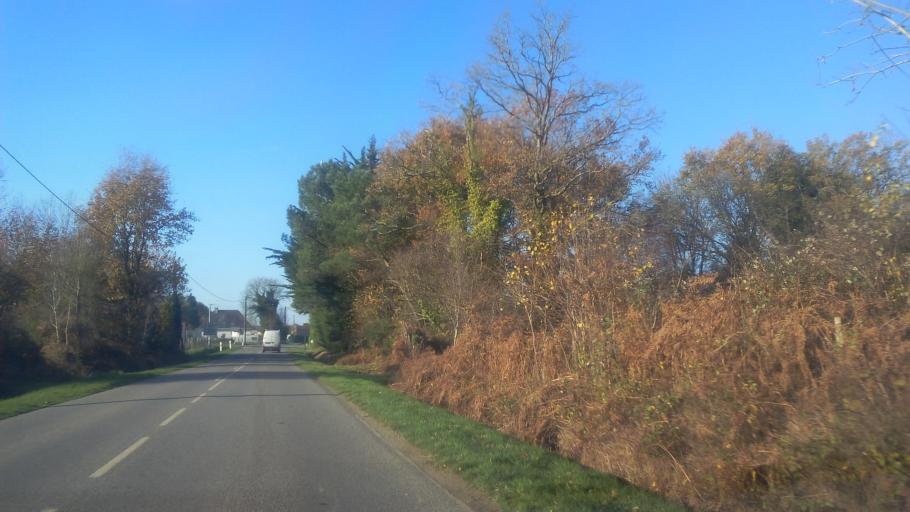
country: FR
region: Brittany
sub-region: Departement du Morbihan
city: Peillac
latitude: 47.7143
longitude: -2.2037
